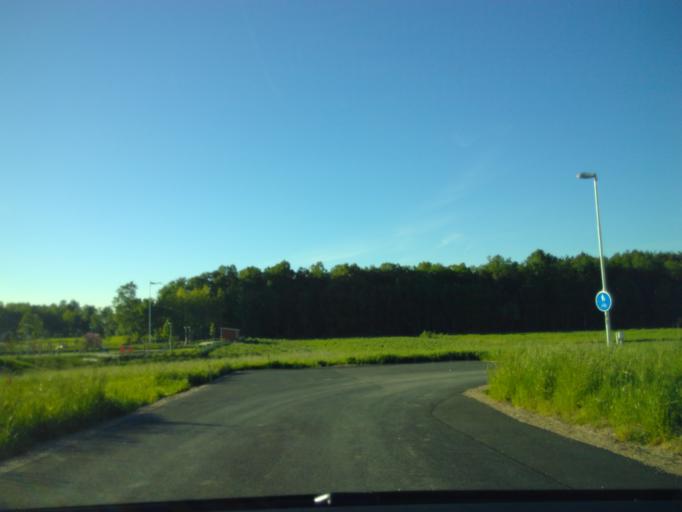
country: SE
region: Vaestra Goetaland
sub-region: Vargarda Kommun
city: Vargarda
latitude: 58.0214
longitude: 12.8188
